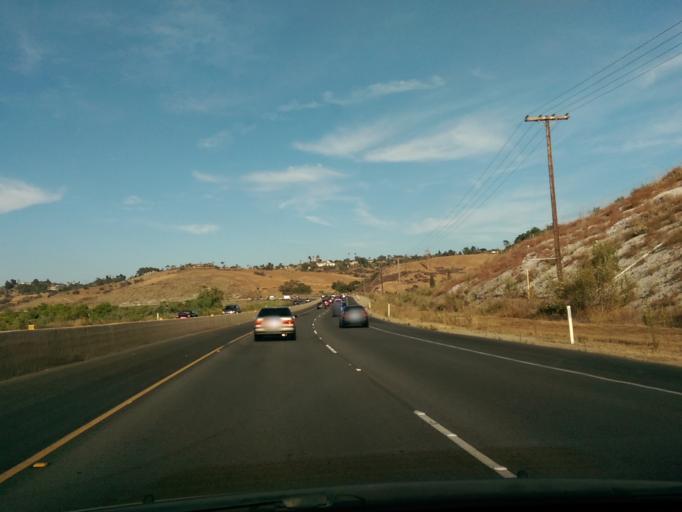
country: US
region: California
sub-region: San Diego County
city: Bonsall
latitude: 33.2542
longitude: -117.2497
